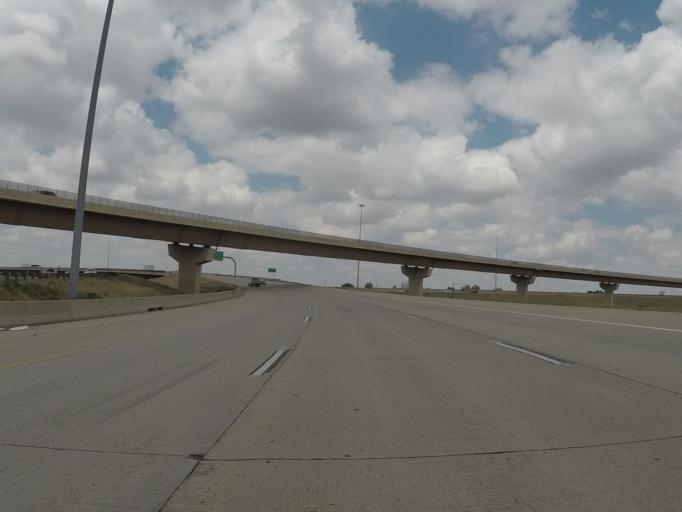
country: US
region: Colorado
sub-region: Adams County
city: Aurora
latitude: 39.7695
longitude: -104.8276
